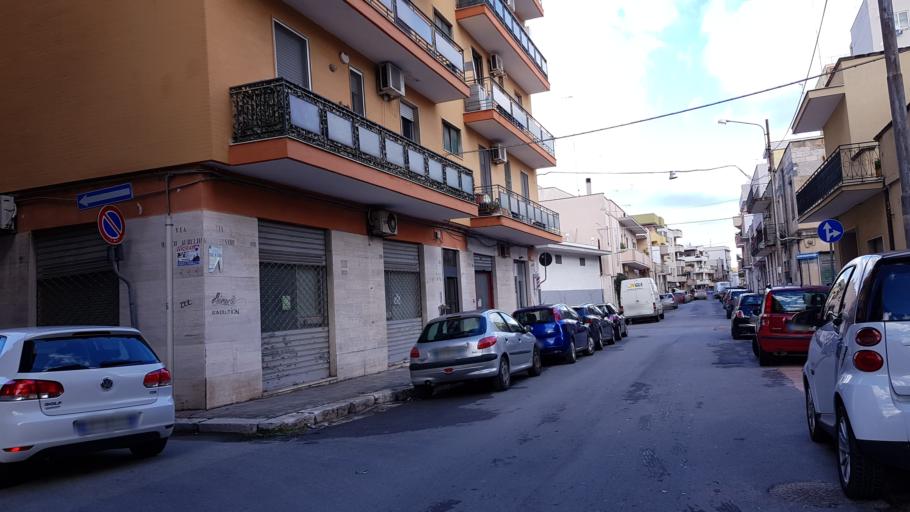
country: IT
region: Apulia
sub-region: Provincia di Brindisi
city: Brindisi
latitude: 40.6327
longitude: 17.9342
